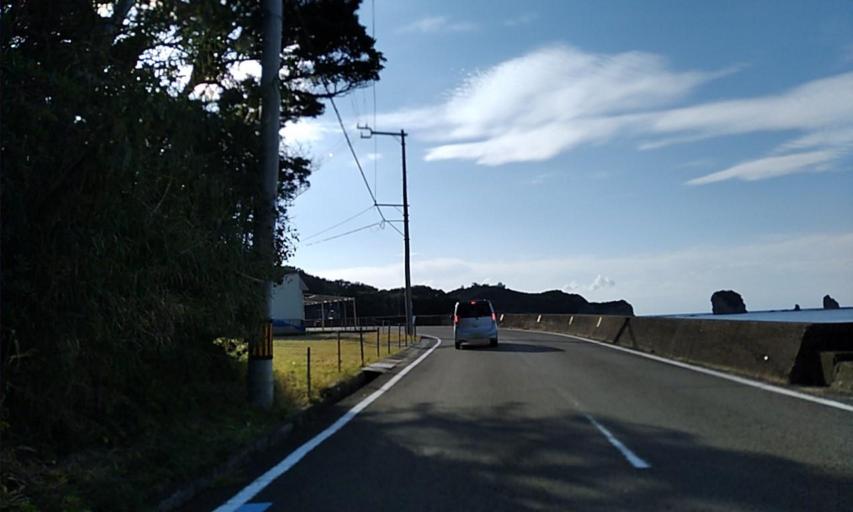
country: JP
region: Wakayama
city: Tanabe
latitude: 33.6942
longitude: 135.3444
